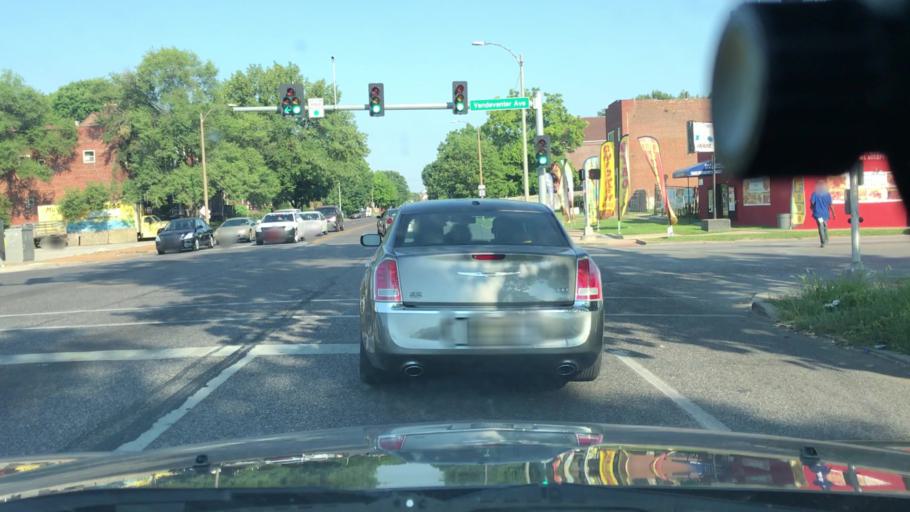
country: US
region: Missouri
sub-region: City of Saint Louis
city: St. Louis
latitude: 38.6488
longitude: -90.2341
